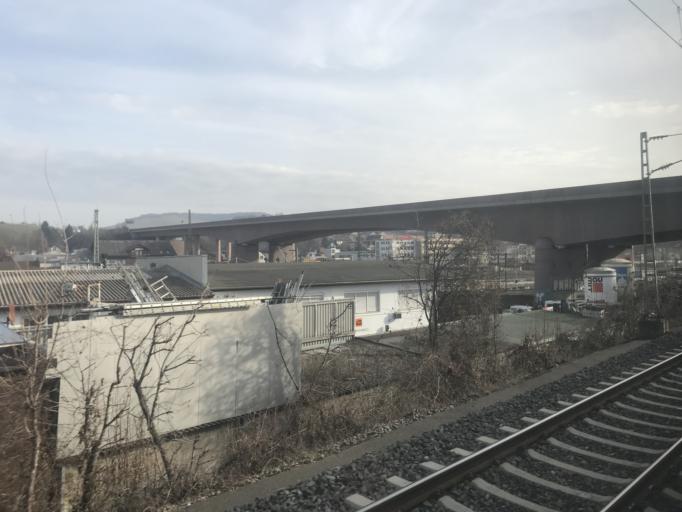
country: DE
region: Baden-Wuerttemberg
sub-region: Regierungsbezirk Stuttgart
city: Stuttgart-Ost
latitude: 48.7910
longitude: 9.2410
